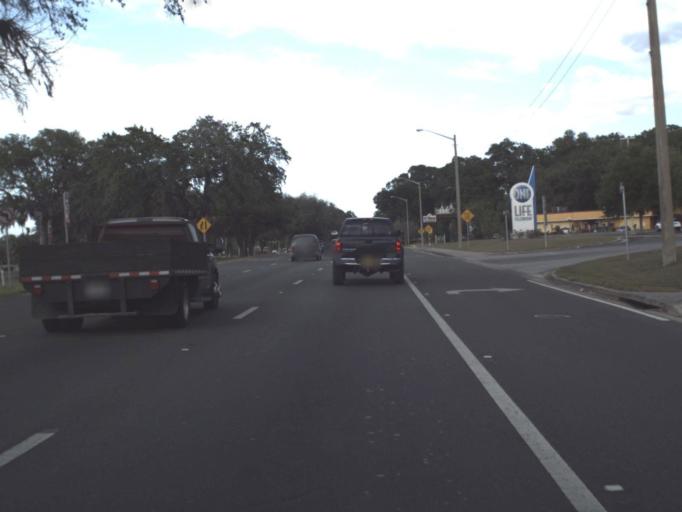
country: US
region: Florida
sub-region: Marion County
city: Ocala
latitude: 29.1980
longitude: -82.0855
